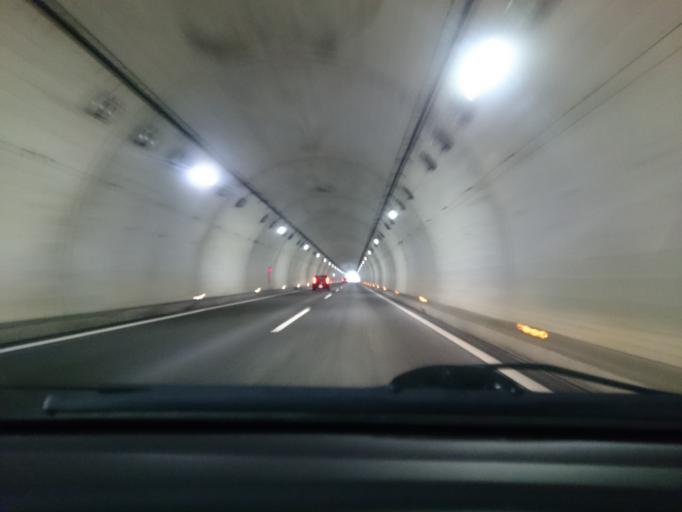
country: JP
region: Fukushima
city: Funehikimachi-funehiki
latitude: 37.3483
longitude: 140.6078
